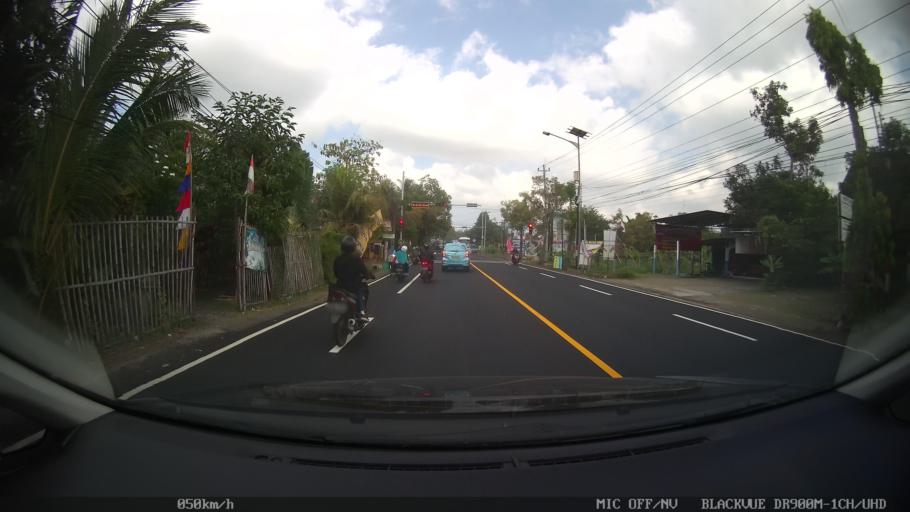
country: ID
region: Daerah Istimewa Yogyakarta
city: Srandakan
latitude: -7.8705
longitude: 110.1428
